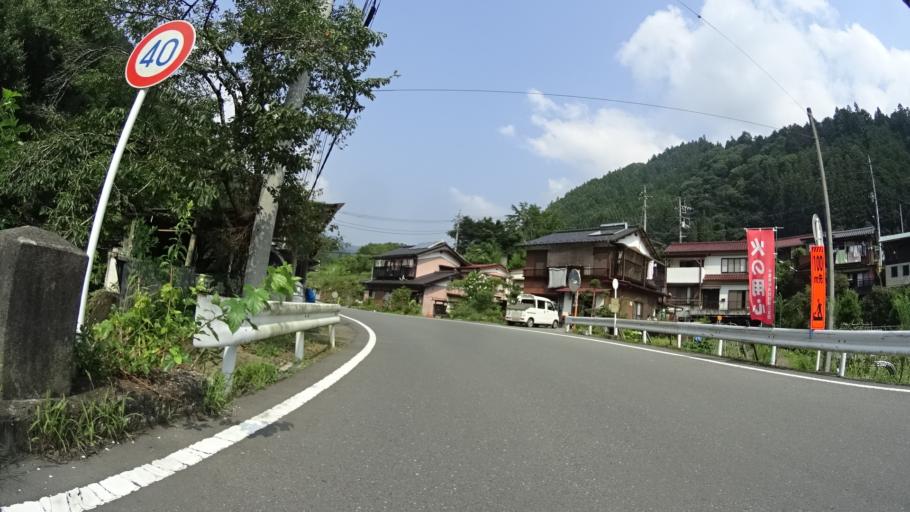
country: JP
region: Saitama
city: Chichibu
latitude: 36.0492
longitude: 138.8810
